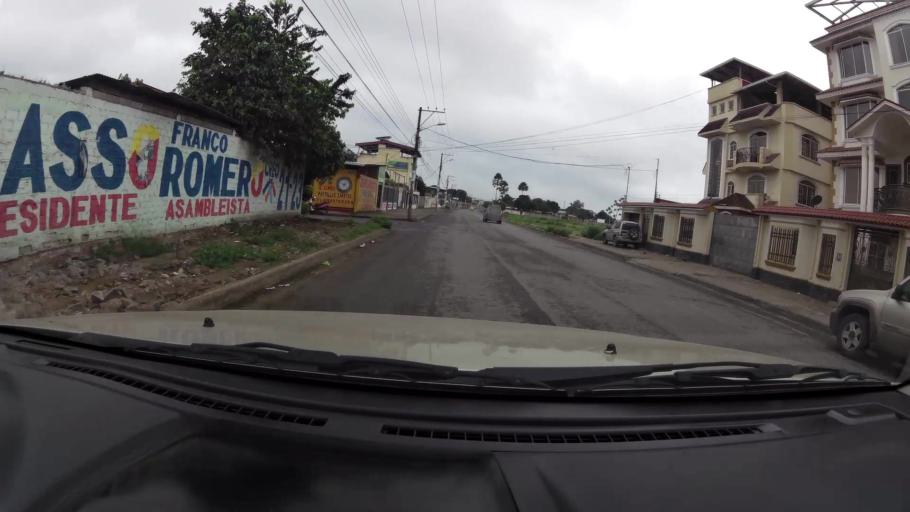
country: EC
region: El Oro
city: Pasaje
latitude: -3.3270
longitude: -79.8165
